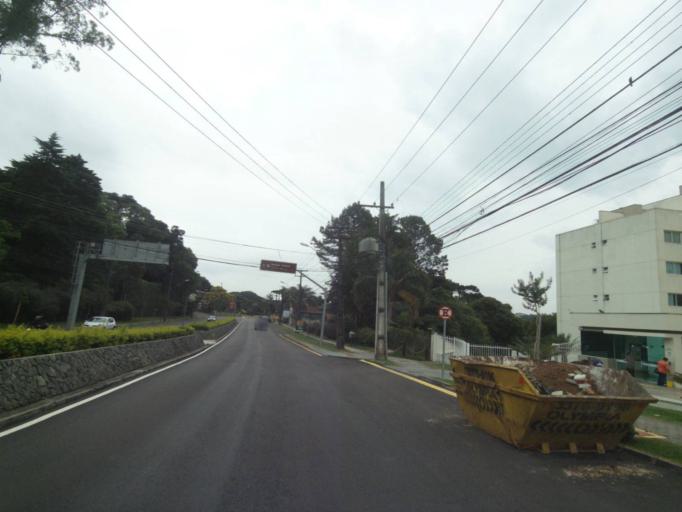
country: BR
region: Parana
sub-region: Curitiba
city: Curitiba
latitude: -25.4154
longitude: -49.2989
